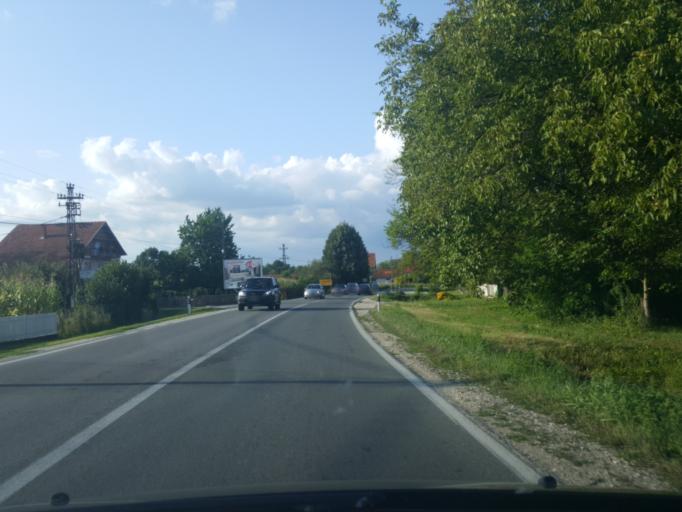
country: RS
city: Lipnicki Sor
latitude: 44.6024
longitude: 19.2543
